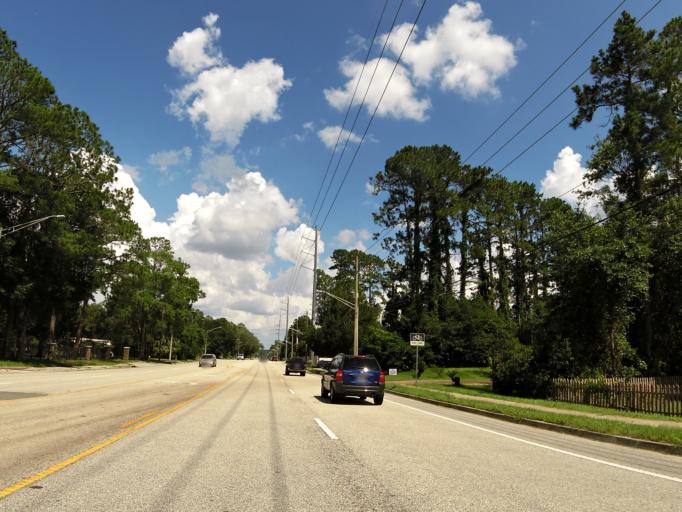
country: US
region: Florida
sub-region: Saint Johns County
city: Fruit Cove
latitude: 30.1556
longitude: -81.5917
